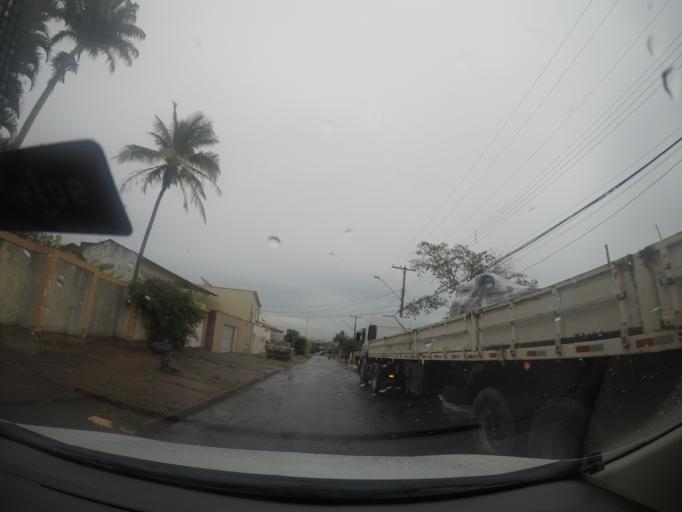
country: BR
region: Goias
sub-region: Goiania
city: Goiania
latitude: -16.6378
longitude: -49.2362
